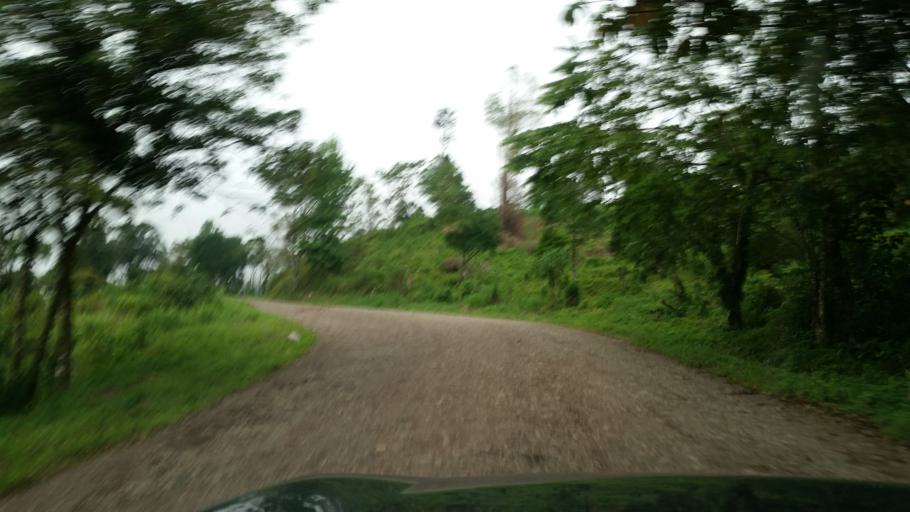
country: NI
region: Jinotega
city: San Jose de Bocay
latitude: 13.2809
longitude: -85.7199
